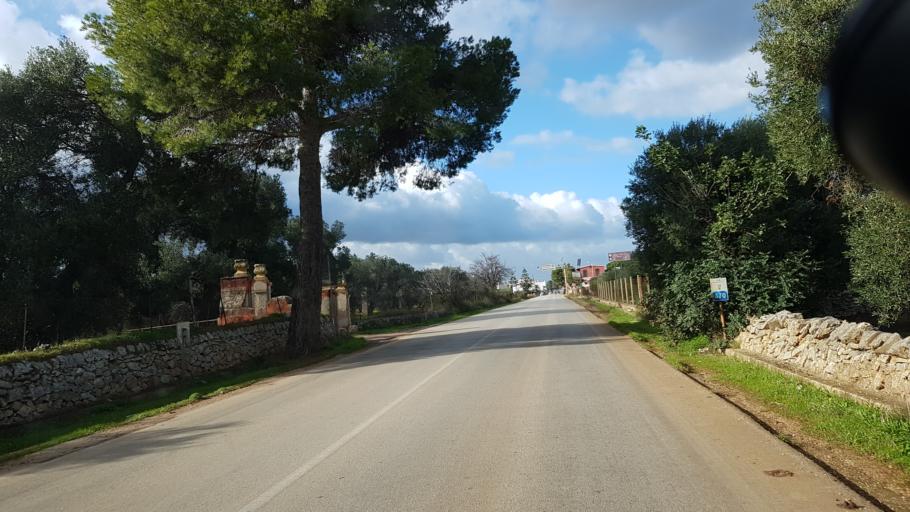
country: IT
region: Apulia
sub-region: Provincia di Brindisi
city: Montalbano
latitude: 40.7796
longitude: 17.4866
